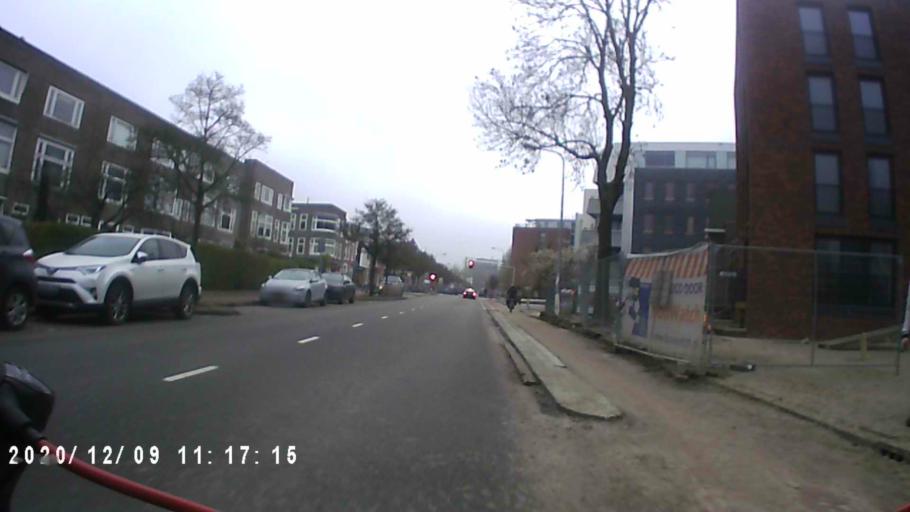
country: NL
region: Groningen
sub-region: Gemeente Groningen
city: Groningen
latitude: 53.2172
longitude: 6.5458
